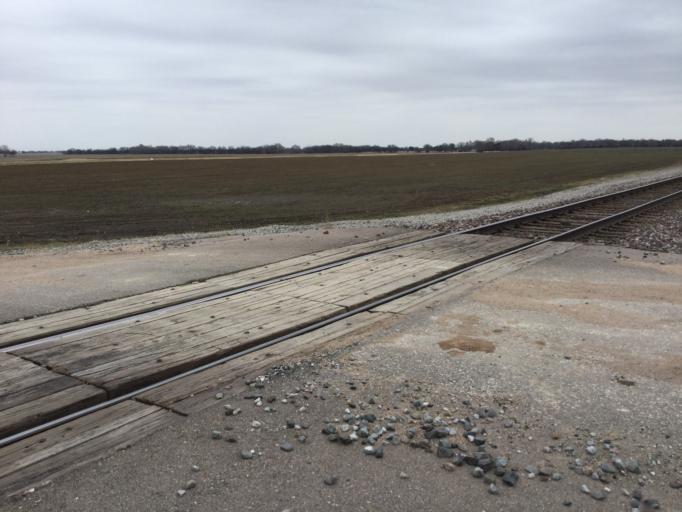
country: US
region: Kansas
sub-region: Sedgwick County
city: Haysville
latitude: 37.4918
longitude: -97.3706
